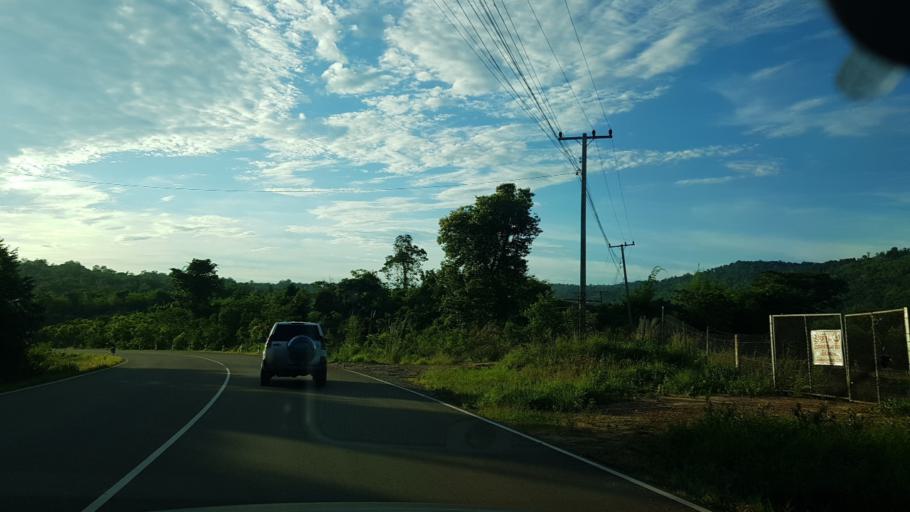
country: TH
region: Nong Khai
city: Sangkhom
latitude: 18.0362
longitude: 102.3647
